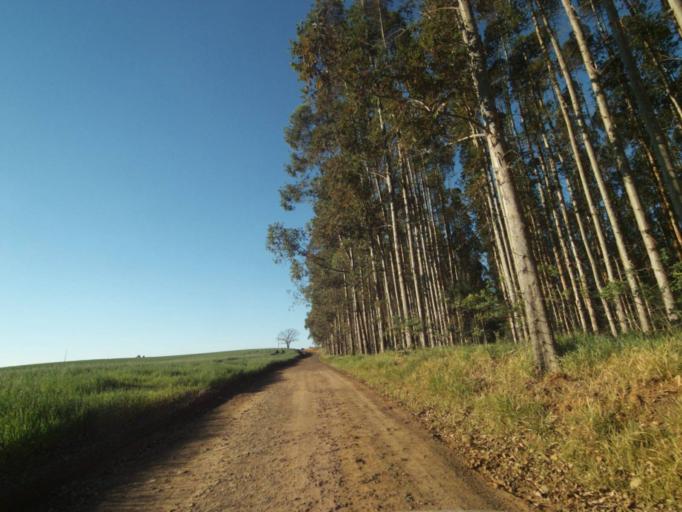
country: BR
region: Parana
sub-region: Telemaco Borba
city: Telemaco Borba
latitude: -24.4877
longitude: -50.5936
